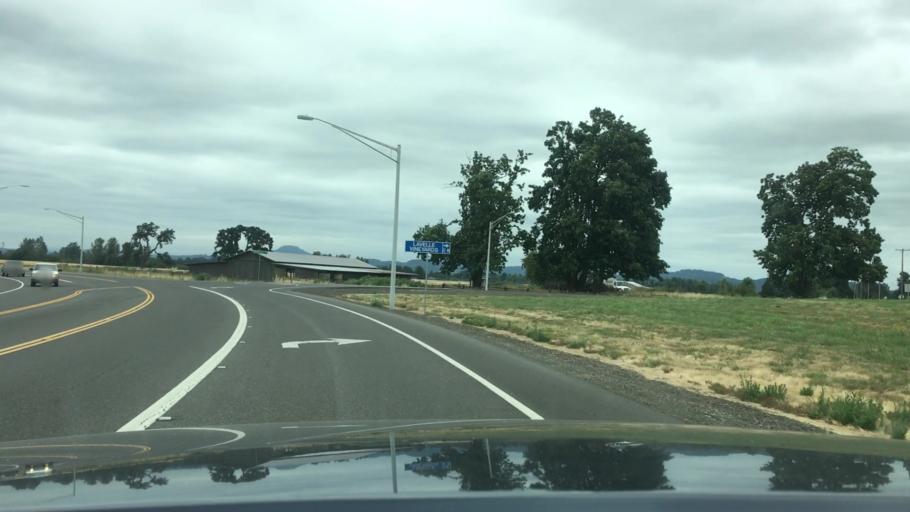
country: US
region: Oregon
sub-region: Lane County
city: Junction City
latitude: 44.1117
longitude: -123.2081
